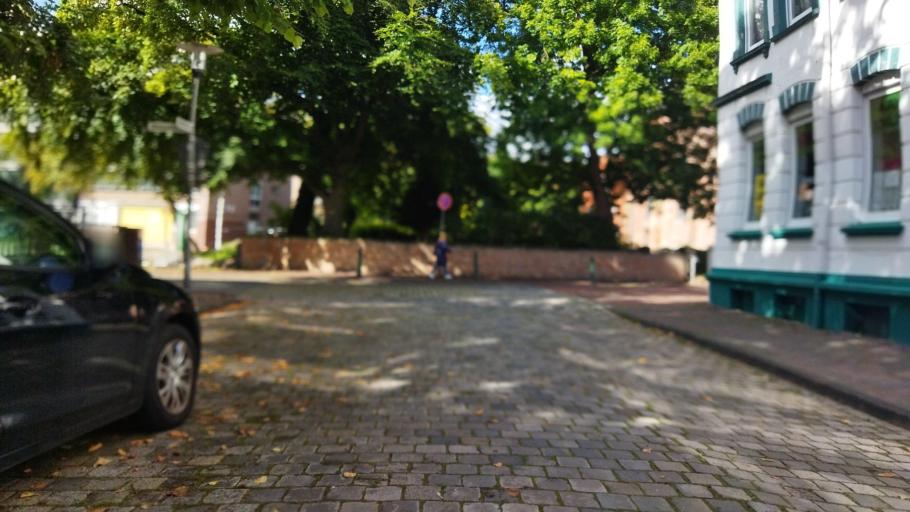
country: DE
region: Lower Saxony
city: Emden
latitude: 53.3651
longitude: 7.2030
